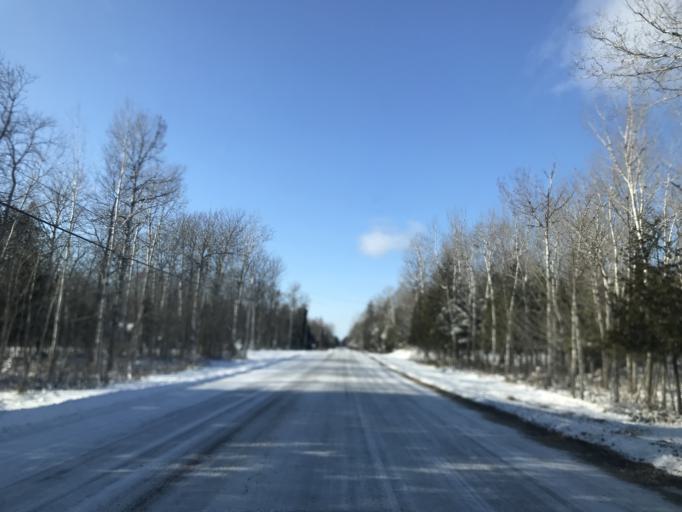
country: US
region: Wisconsin
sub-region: Door County
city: Sturgeon Bay
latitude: 44.8496
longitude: -87.4856
